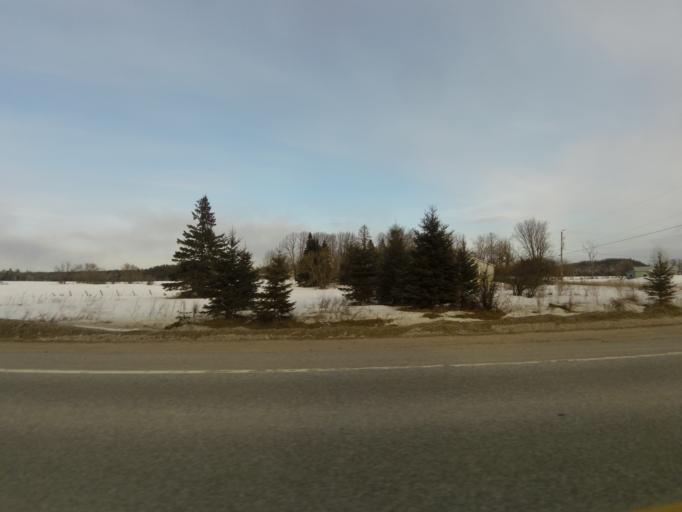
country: CA
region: Quebec
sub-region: Outaouais
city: Wakefield
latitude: 45.8727
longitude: -76.0241
